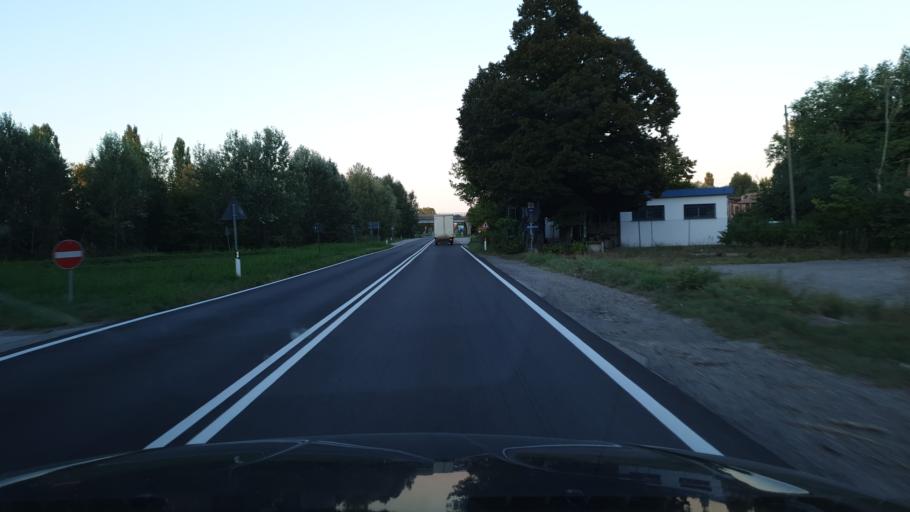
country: IT
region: Emilia-Romagna
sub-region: Provincia di Bologna
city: Granarolo dell'Emilia e Viadagola
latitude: 44.5791
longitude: 11.4156
